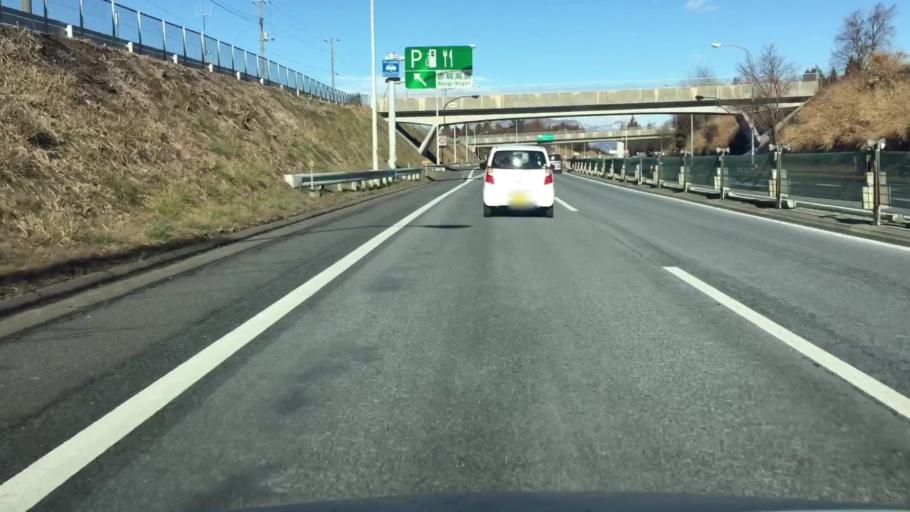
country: JP
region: Gunma
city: Numata
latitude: 36.5985
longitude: 139.0637
